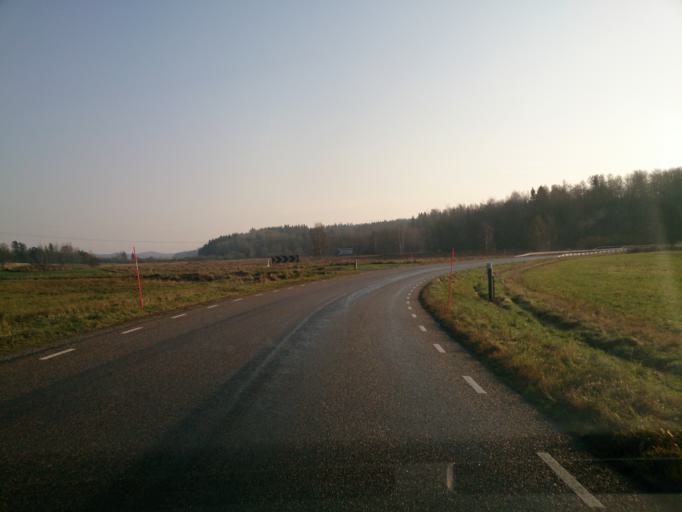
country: SE
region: OEstergoetland
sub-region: Atvidabergs Kommun
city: Atvidaberg
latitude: 58.2854
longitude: 16.0337
